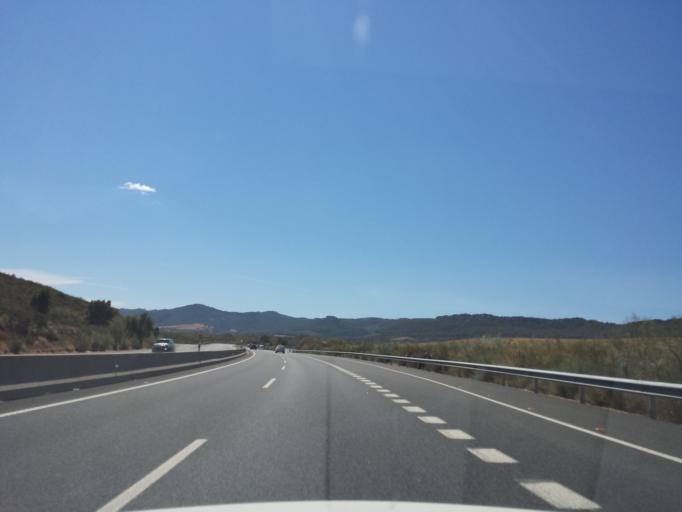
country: ES
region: Extremadura
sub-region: Provincia de Caceres
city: Casas de Miravete
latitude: 39.7349
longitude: -5.7227
